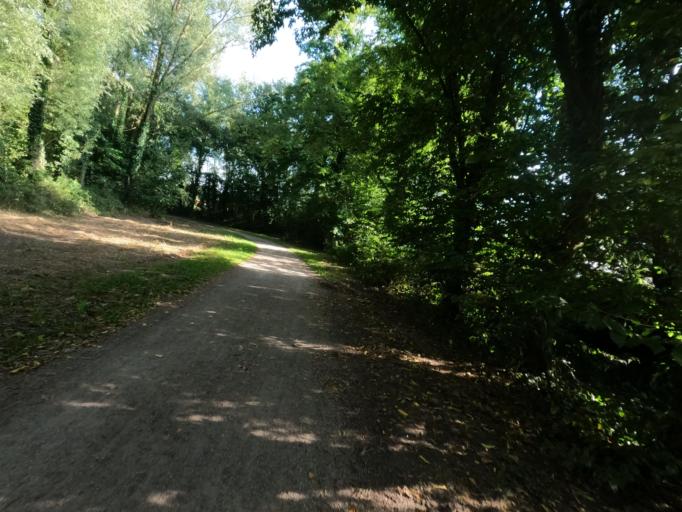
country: DE
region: North Rhine-Westphalia
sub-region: Regierungsbezirk Dusseldorf
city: Bruggen
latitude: 51.2360
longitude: 6.1574
